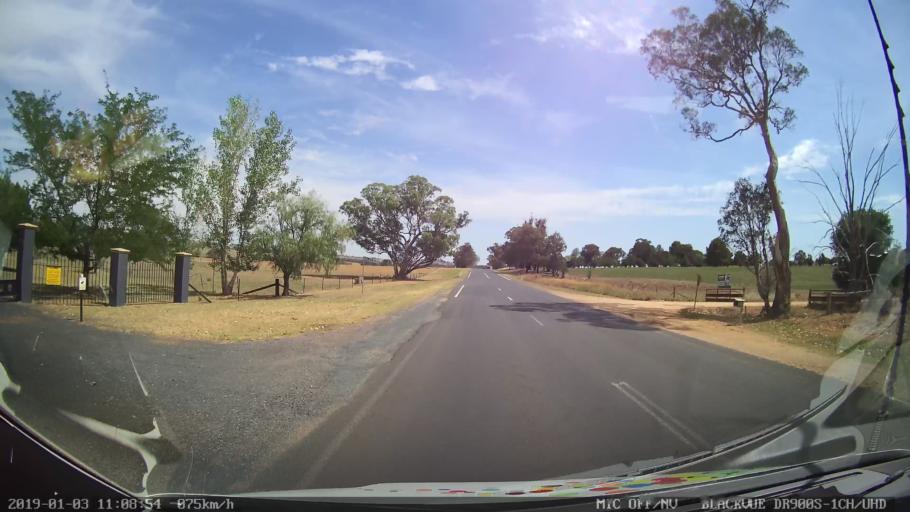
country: AU
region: New South Wales
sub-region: Young
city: Young
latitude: -34.2444
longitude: 148.2557
